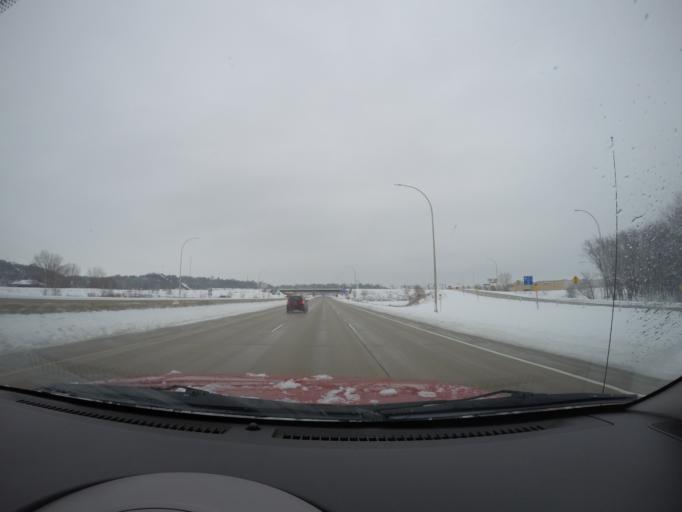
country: US
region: Minnesota
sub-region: Olmsted County
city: Rochester
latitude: 43.9990
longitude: -92.4842
